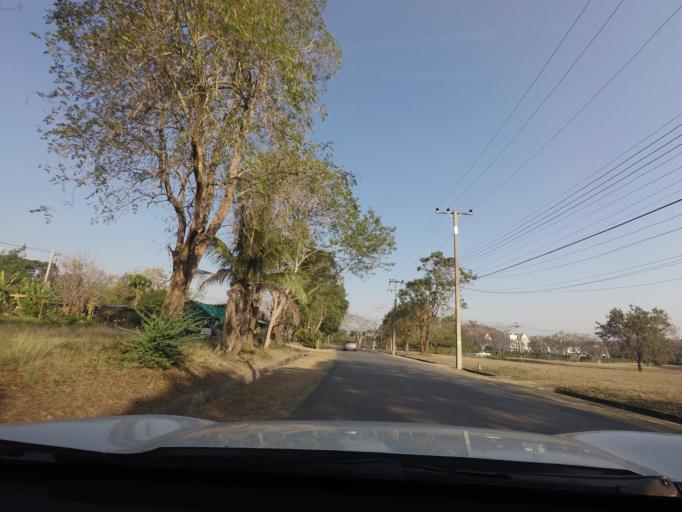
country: TH
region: Nakhon Ratchasima
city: Pak Chong
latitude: 14.5883
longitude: 101.4442
